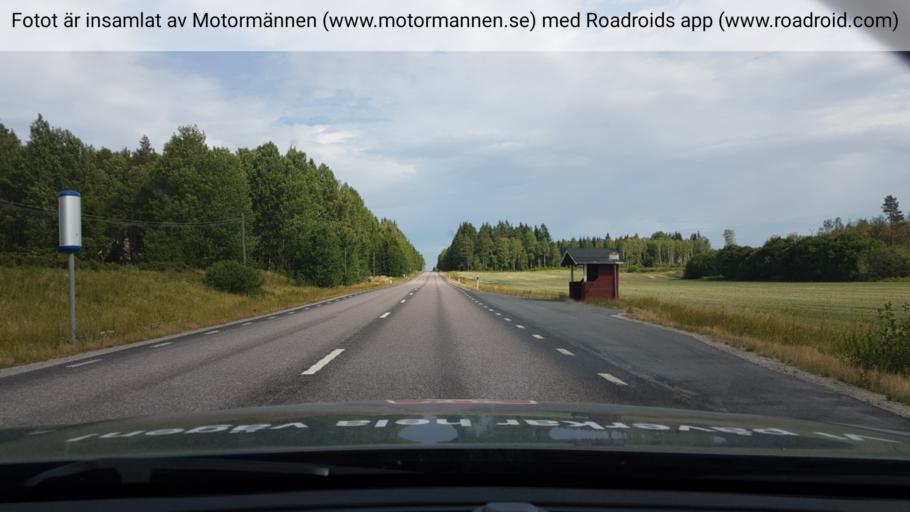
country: SE
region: Uppsala
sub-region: Enkopings Kommun
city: Orsundsbro
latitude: 59.8699
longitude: 17.3133
